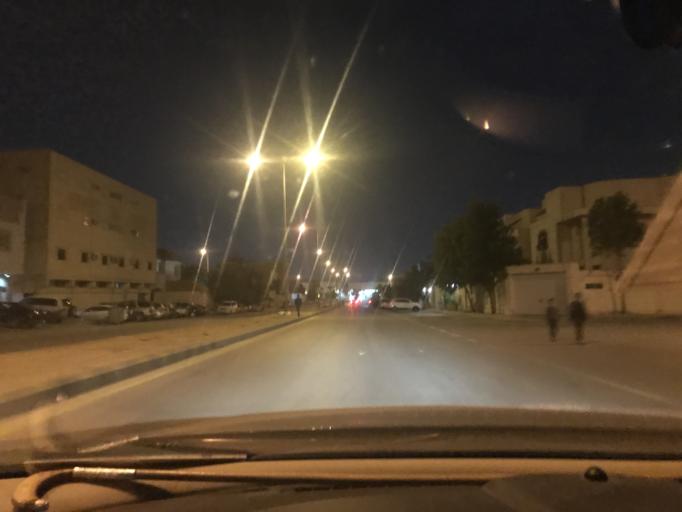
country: SA
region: Ar Riyad
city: Riyadh
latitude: 24.7576
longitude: 46.7474
